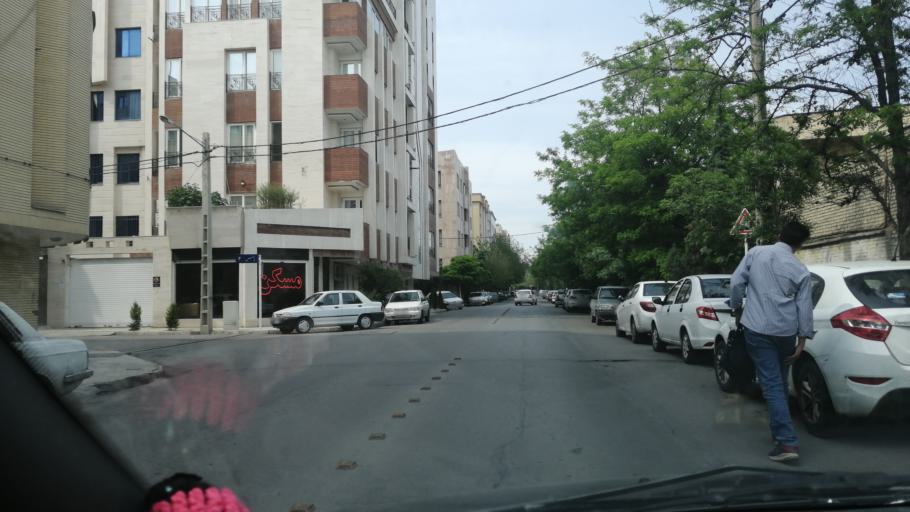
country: IR
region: Razavi Khorasan
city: Mashhad
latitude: 36.3252
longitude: 59.5669
